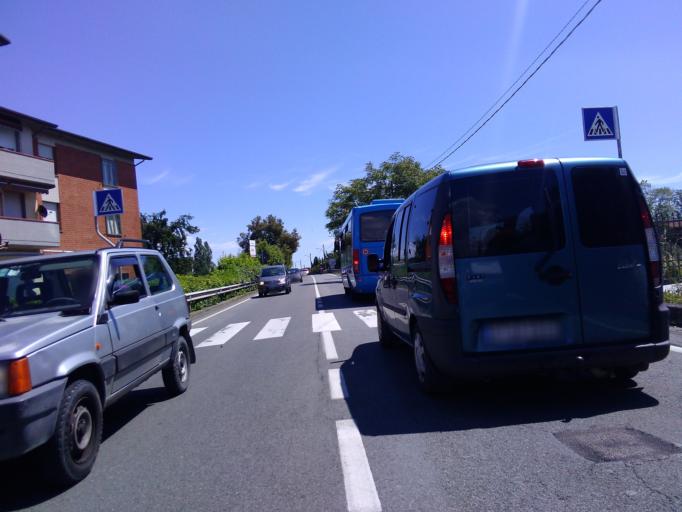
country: IT
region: Liguria
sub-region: Provincia di La Spezia
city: Santo Stefano di Magra
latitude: 44.1502
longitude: 9.9209
